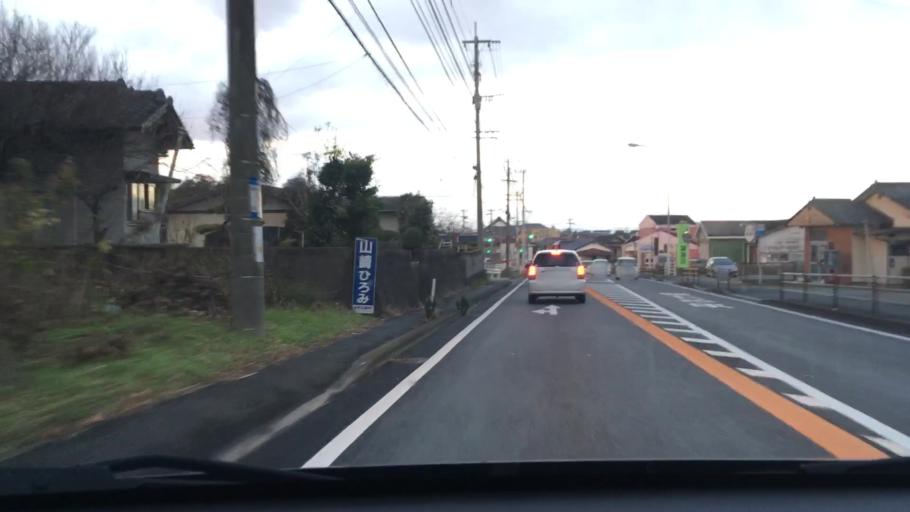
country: JP
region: Fukuoka
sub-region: Buzen-shi
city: Buzen
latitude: 33.6207
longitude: 131.0954
